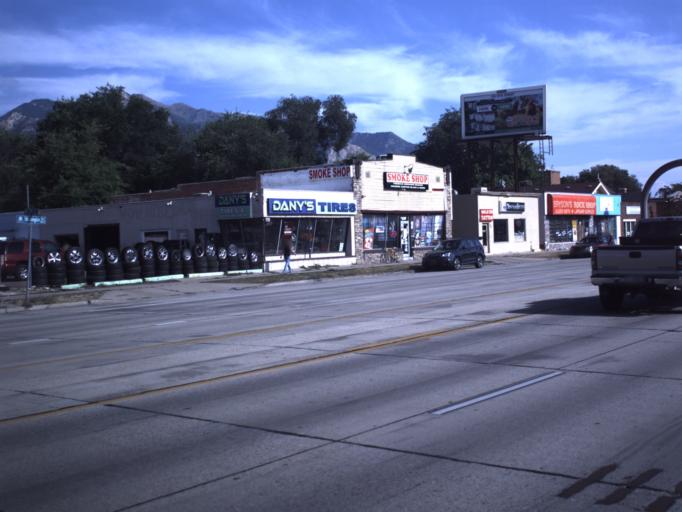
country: US
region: Utah
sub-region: Weber County
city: Harrisville
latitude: 41.2580
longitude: -111.9698
